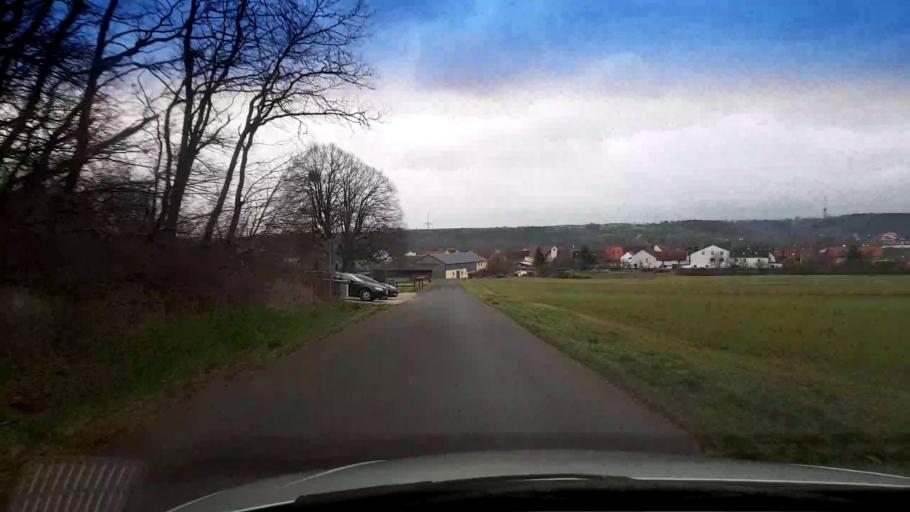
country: DE
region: Bavaria
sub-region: Upper Franconia
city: Viereth-Trunstadt
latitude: 49.9399
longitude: 10.7878
